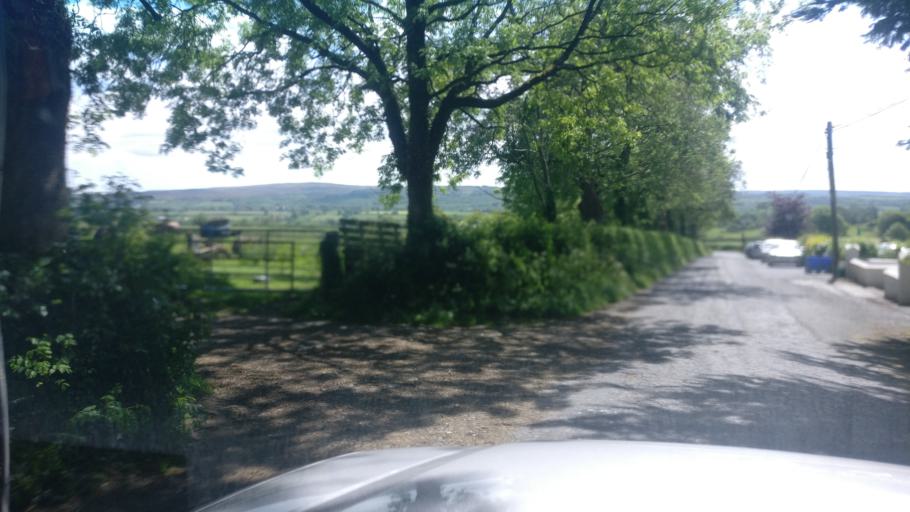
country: IE
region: Connaught
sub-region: County Galway
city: Gort
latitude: 53.1471
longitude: -8.7420
